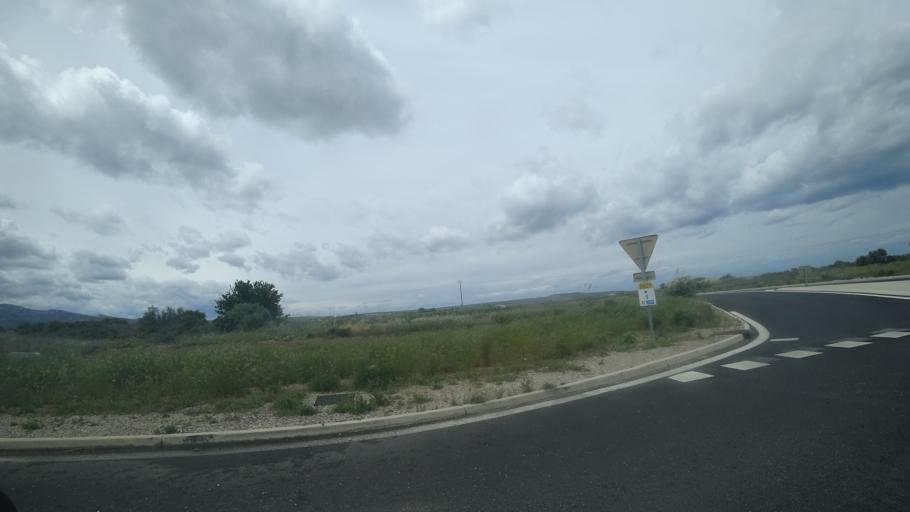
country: FR
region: Languedoc-Roussillon
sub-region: Departement de l'Aude
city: Leucate
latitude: 42.9339
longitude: 3.0028
